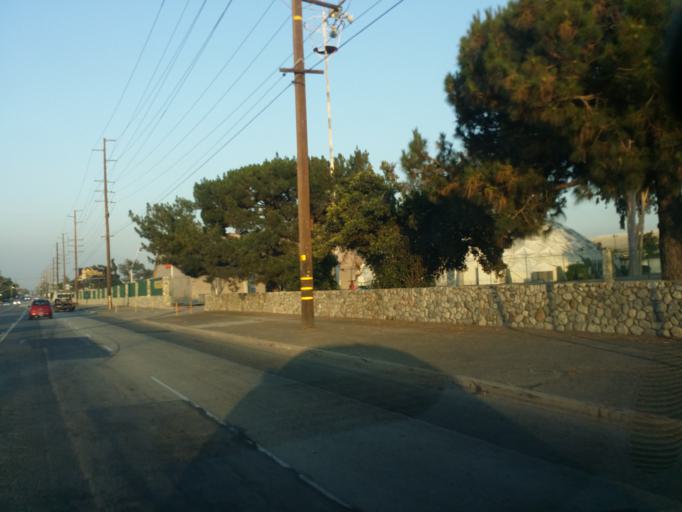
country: US
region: California
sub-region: San Bernardino County
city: San Bernardino
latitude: 34.0922
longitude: -117.2929
